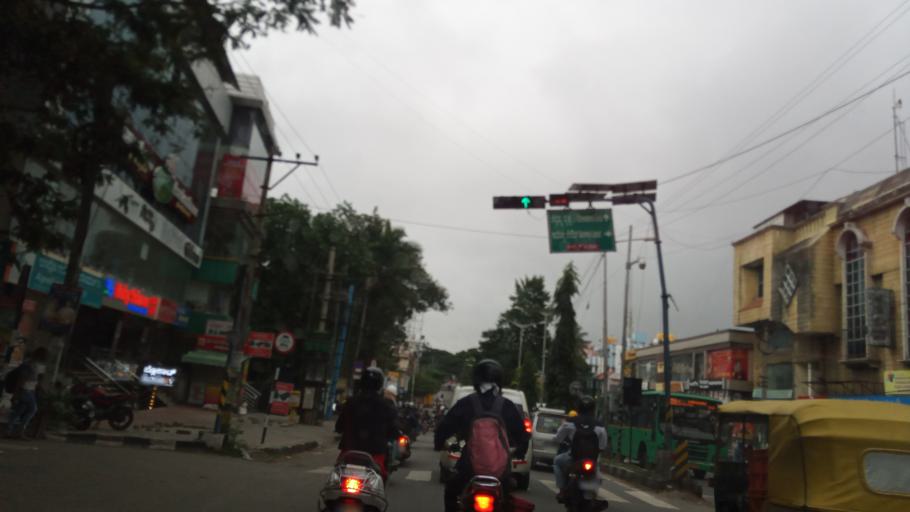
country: IN
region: Karnataka
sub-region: Bangalore Urban
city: Bangalore
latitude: 12.9240
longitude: 77.5532
